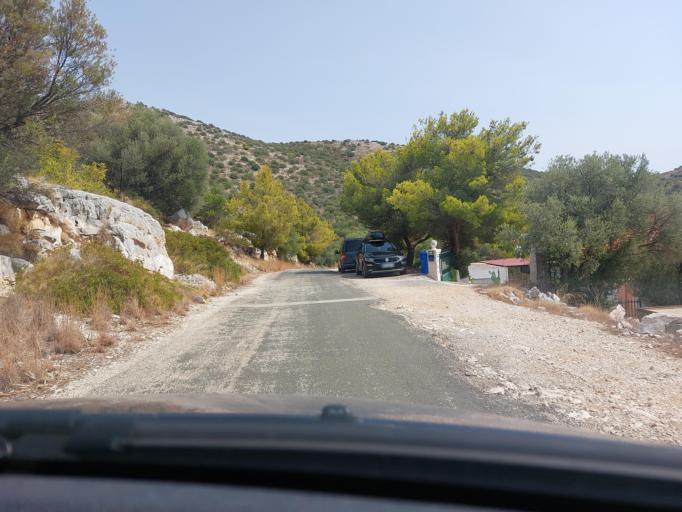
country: HR
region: Dubrovacko-Neretvanska
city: Smokvica
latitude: 42.7347
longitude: 16.8907
